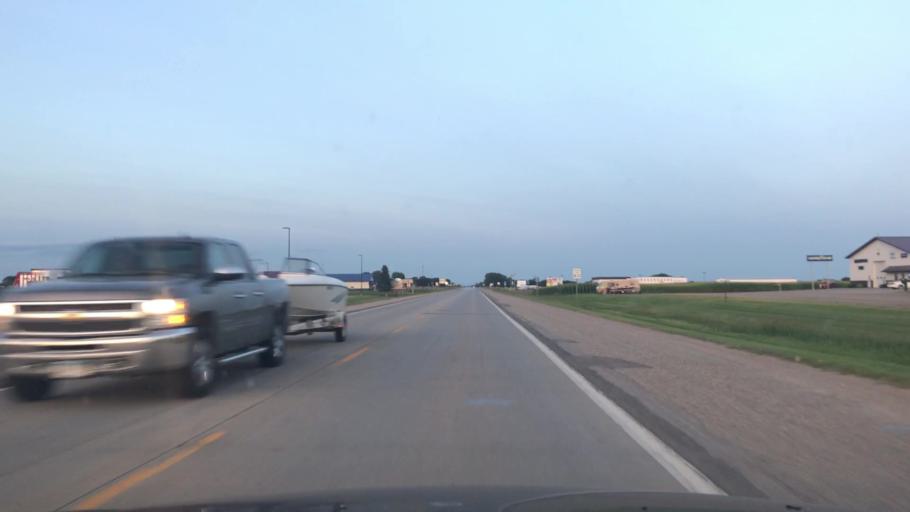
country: US
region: Minnesota
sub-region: Redwood County
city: Redwood Falls
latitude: 44.5414
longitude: -95.0826
